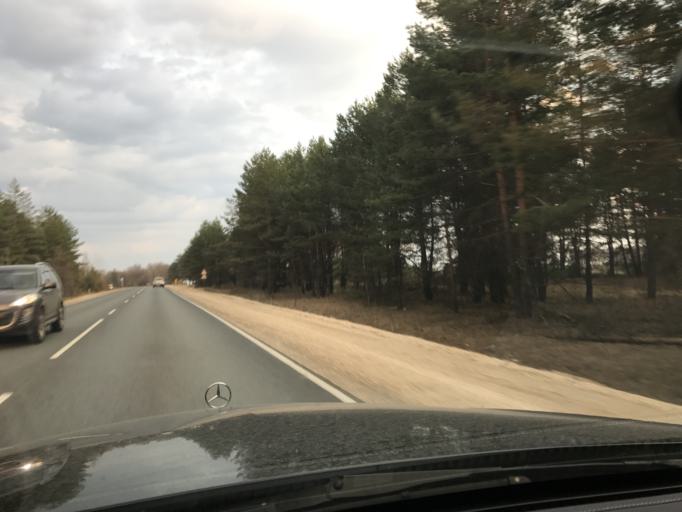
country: RU
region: Vladimir
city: Murom
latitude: 55.6205
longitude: 41.9141
